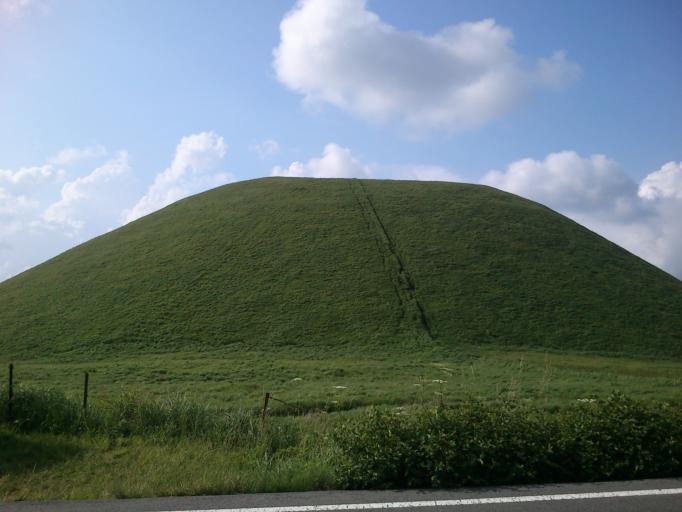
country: JP
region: Kumamoto
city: Aso
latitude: 32.9025
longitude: 131.0444
